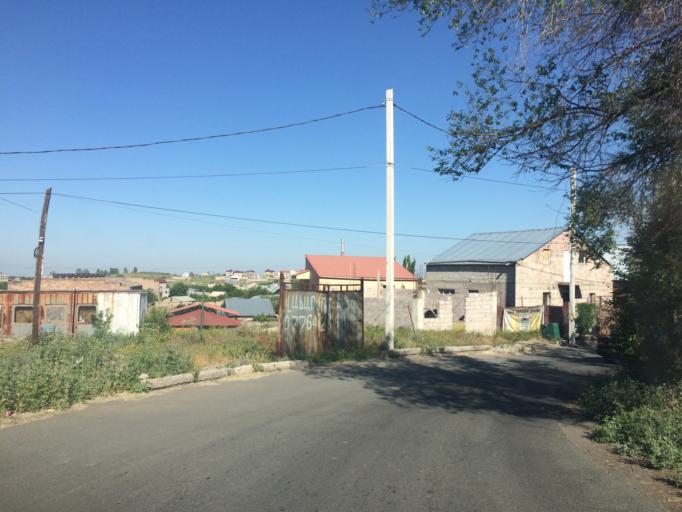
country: AM
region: Yerevan
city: K'anak'erravan
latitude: 40.2214
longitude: 44.5304
